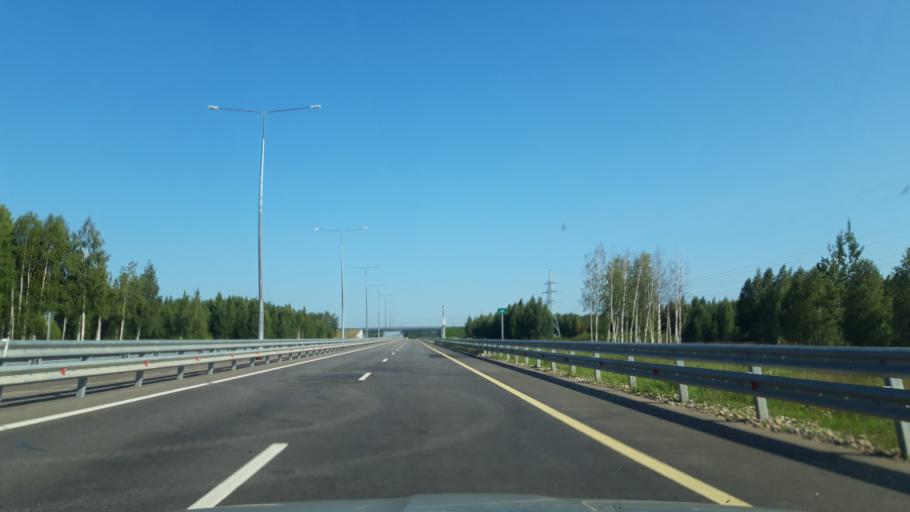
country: RU
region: Tverskaya
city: Zavidovo
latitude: 56.5431
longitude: 36.4922
